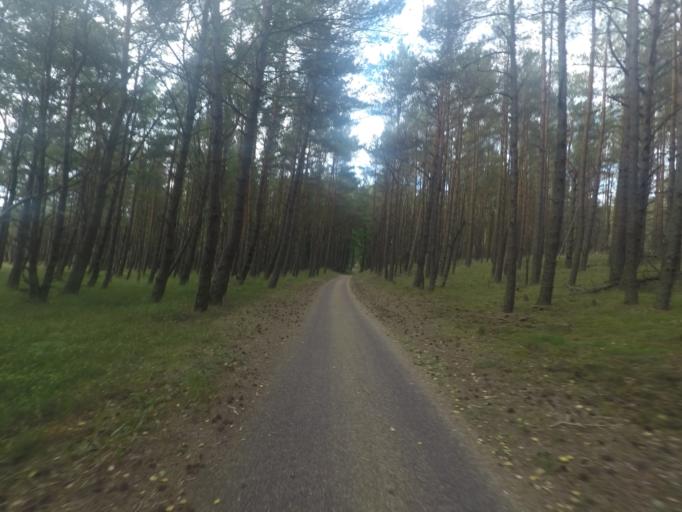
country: LT
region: Klaipedos apskritis
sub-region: Klaipeda
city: Klaipeda
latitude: 55.6605
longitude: 21.1071
